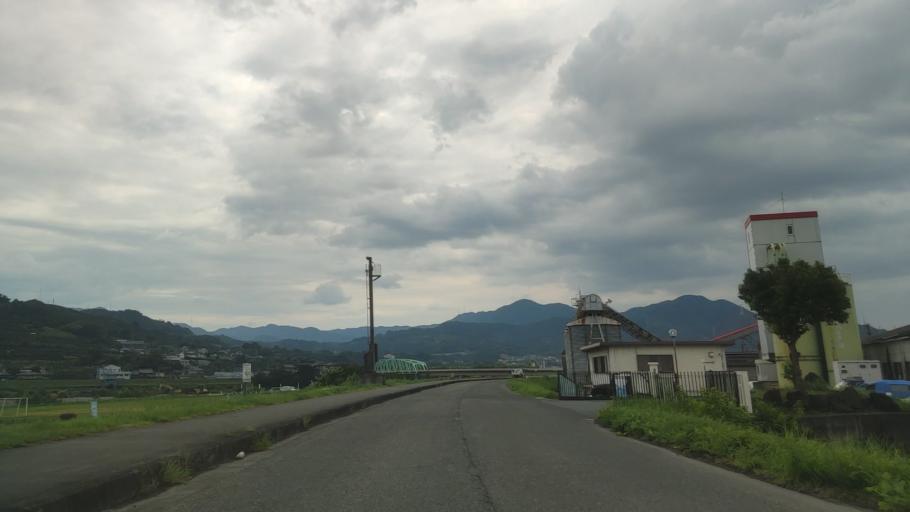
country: JP
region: Wakayama
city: Hashimoto
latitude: 34.3018
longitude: 135.5808
